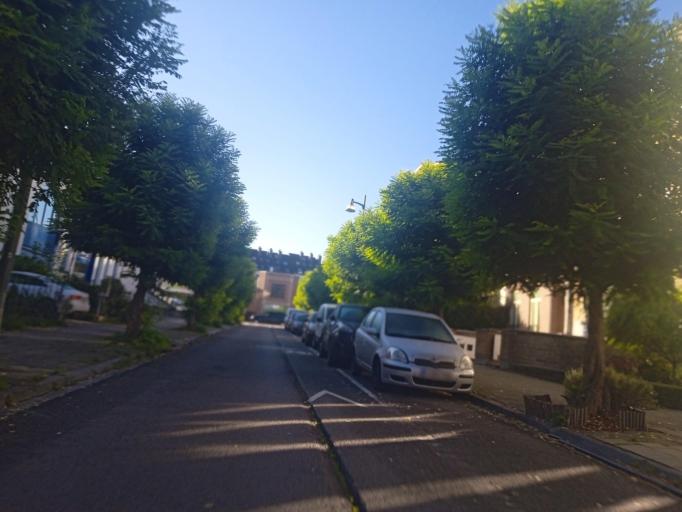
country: BE
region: Brussels Capital
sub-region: Bruxelles-Capitale
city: Brussels
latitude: 50.8483
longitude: 4.3076
